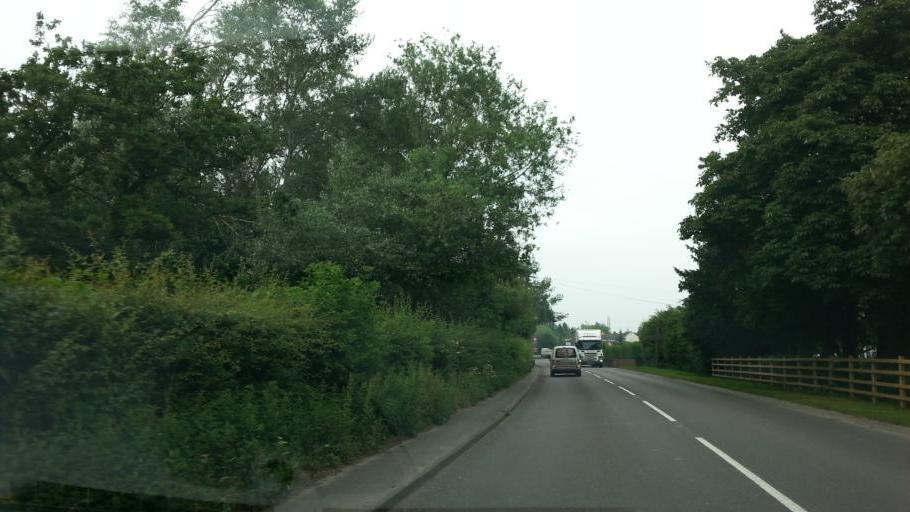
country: GB
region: England
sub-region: Staffordshire
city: Uttoxeter
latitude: 52.8678
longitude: -1.7621
